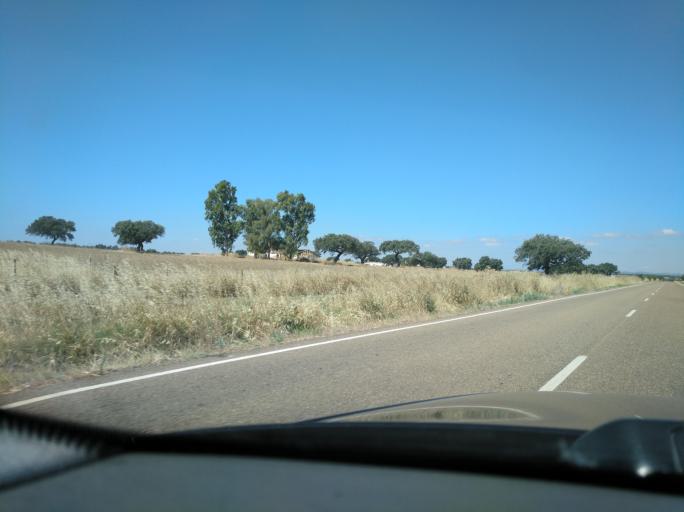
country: ES
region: Extremadura
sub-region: Provincia de Badajoz
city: Olivenza
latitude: 38.7018
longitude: -7.1573
